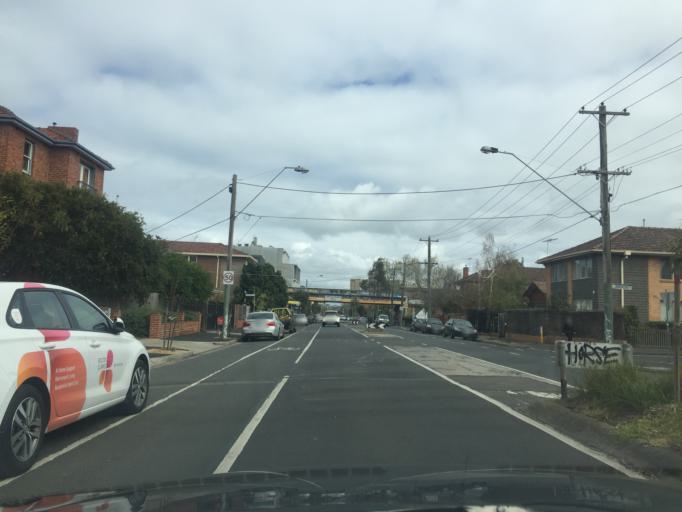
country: AU
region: Victoria
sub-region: Port Phillip
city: Balaclava
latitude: -37.8659
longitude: 144.9954
